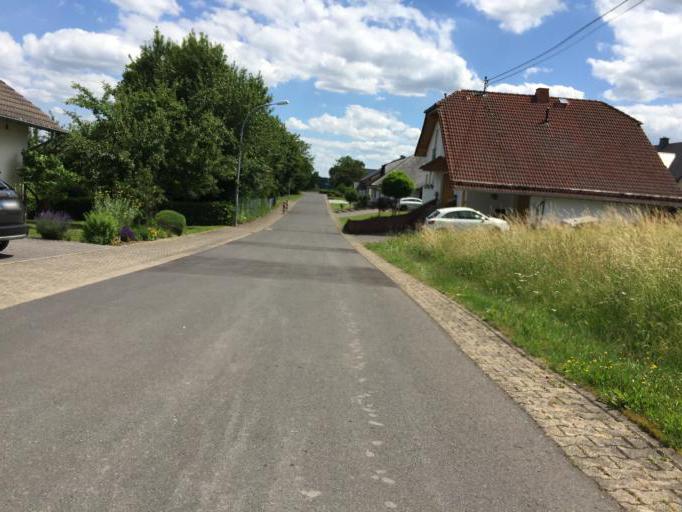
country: DE
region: Rheinland-Pfalz
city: Berod bei Wallmerod
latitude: 50.4759
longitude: 7.9220
